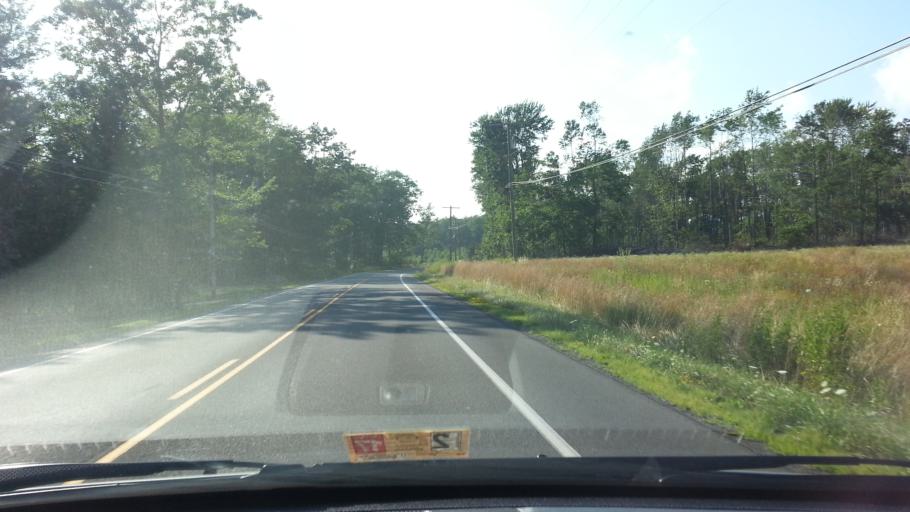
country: US
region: Pennsylvania
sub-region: Elk County
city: Saint Marys
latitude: 41.3576
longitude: -78.5491
